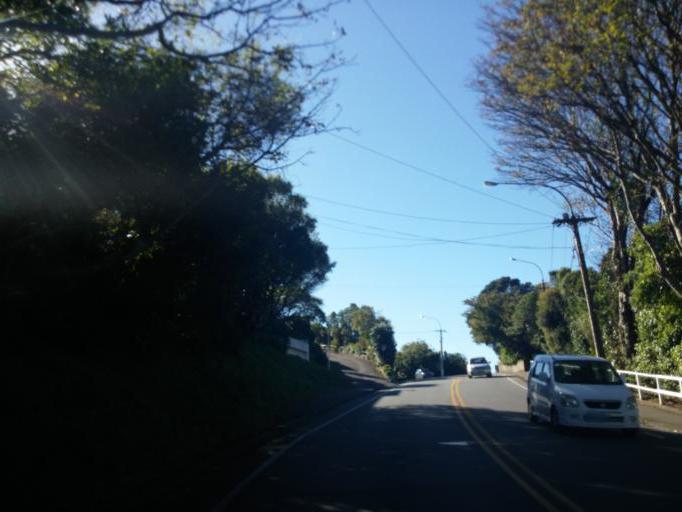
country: NZ
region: Wellington
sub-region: Wellington City
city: Wellington
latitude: -41.2389
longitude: 174.7966
